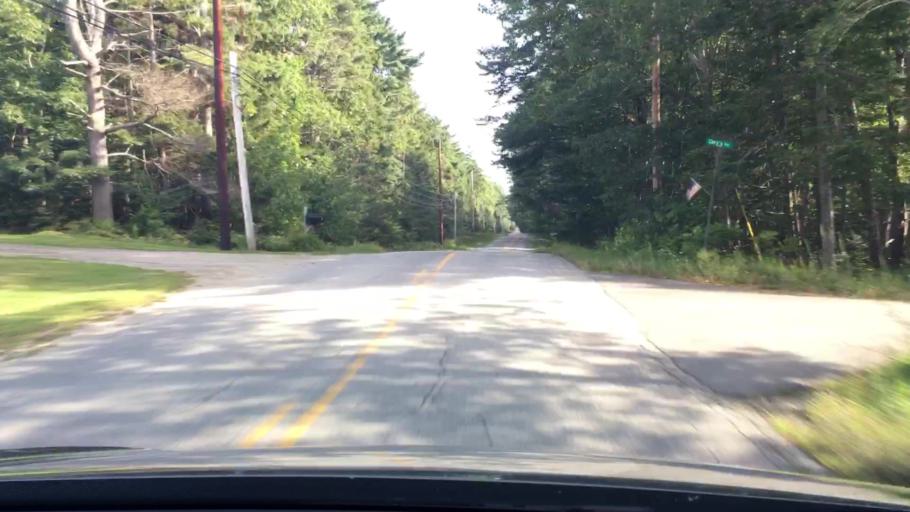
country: US
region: Maine
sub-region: Hancock County
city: Bucksport
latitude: 44.5364
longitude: -68.7940
